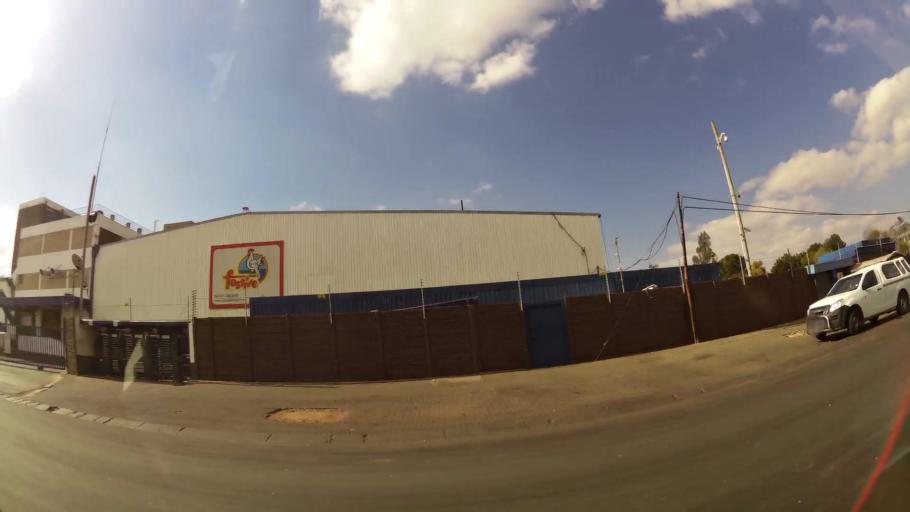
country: ZA
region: Gauteng
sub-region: Ekurhuleni Metropolitan Municipality
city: Tembisa
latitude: -25.9690
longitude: 28.2350
